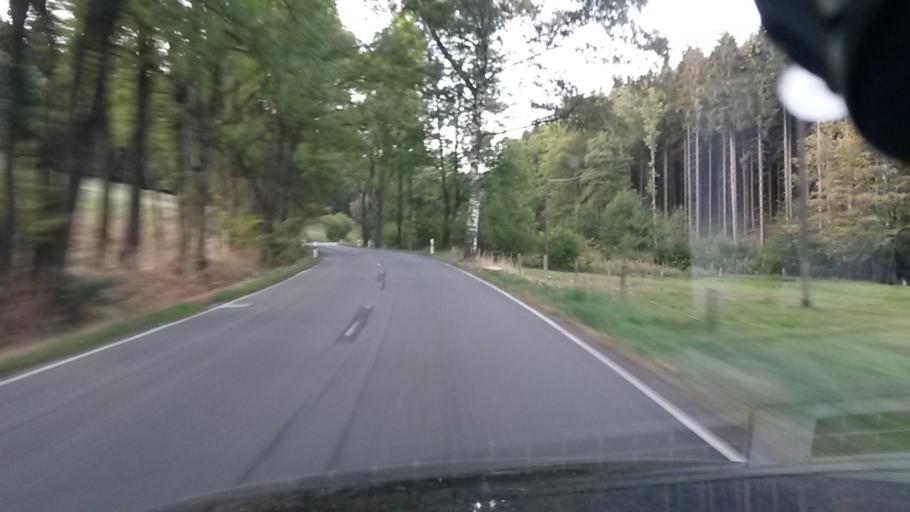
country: DE
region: North Rhine-Westphalia
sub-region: Regierungsbezirk Koln
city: Marienheide
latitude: 51.0619
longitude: 7.5147
